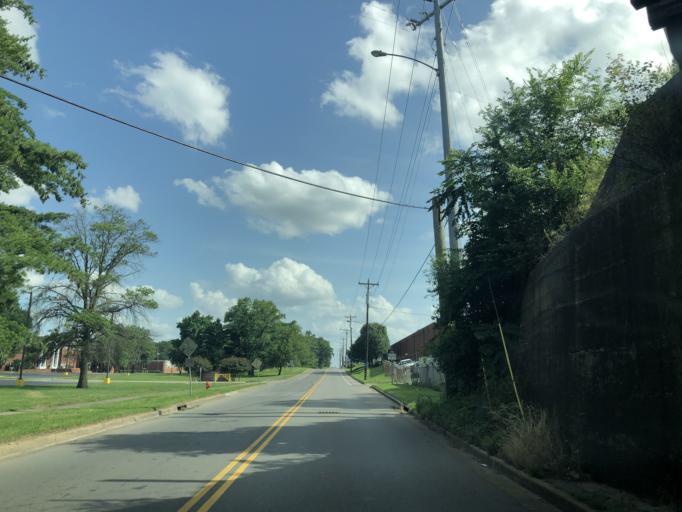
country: US
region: Tennessee
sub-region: Davidson County
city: Nashville
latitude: 36.1367
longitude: -86.7412
